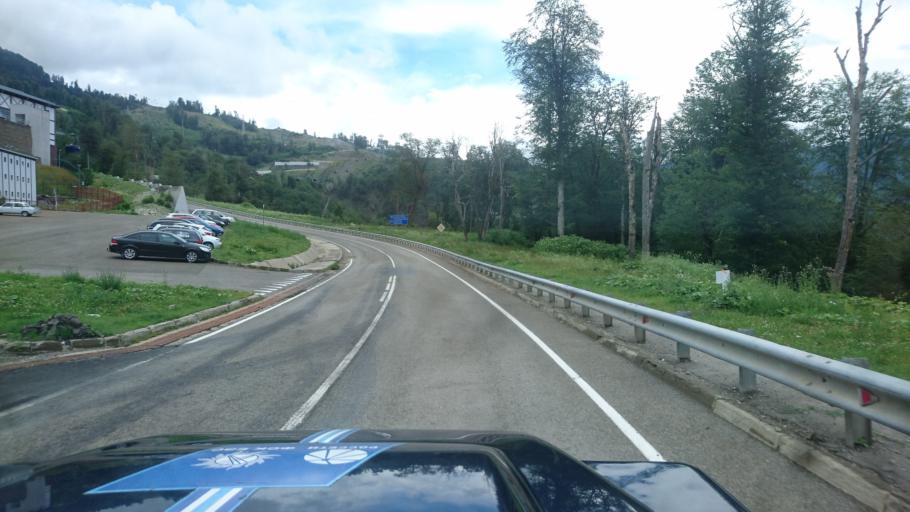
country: RU
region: Krasnodarskiy
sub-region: Sochi City
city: Krasnaya Polyana
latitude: 43.6481
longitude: 40.3397
